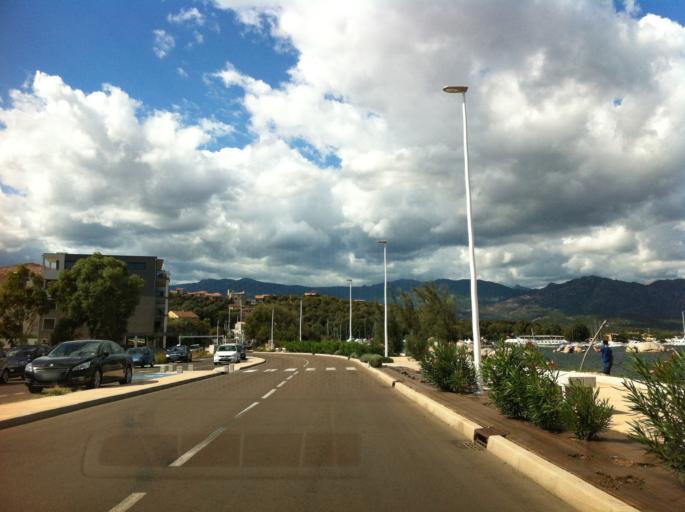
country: FR
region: Corsica
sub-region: Departement de la Corse-du-Sud
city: Porto-Vecchio
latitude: 41.5879
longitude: 9.2885
